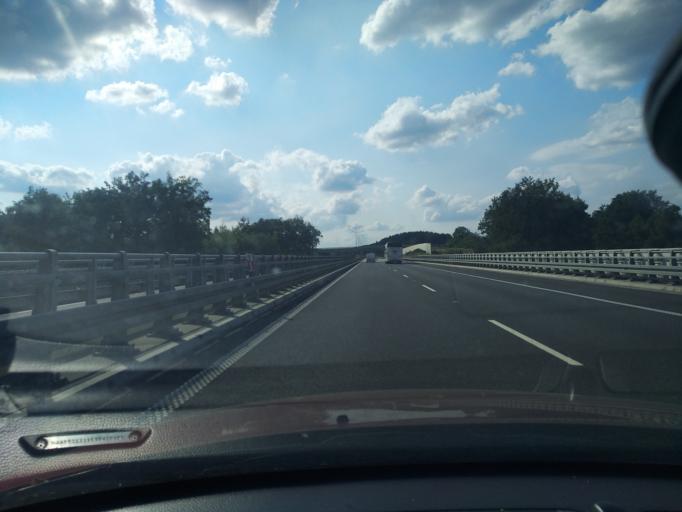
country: PL
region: Lower Silesian Voivodeship
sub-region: Powiat boleslawiecki
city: Nowogrodziec
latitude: 51.2689
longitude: 15.4168
